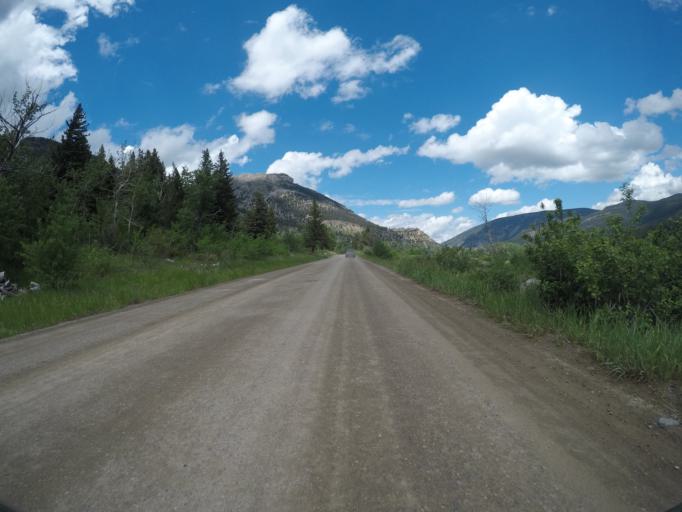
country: US
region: Montana
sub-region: Park County
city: Livingston
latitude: 45.5194
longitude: -110.2254
